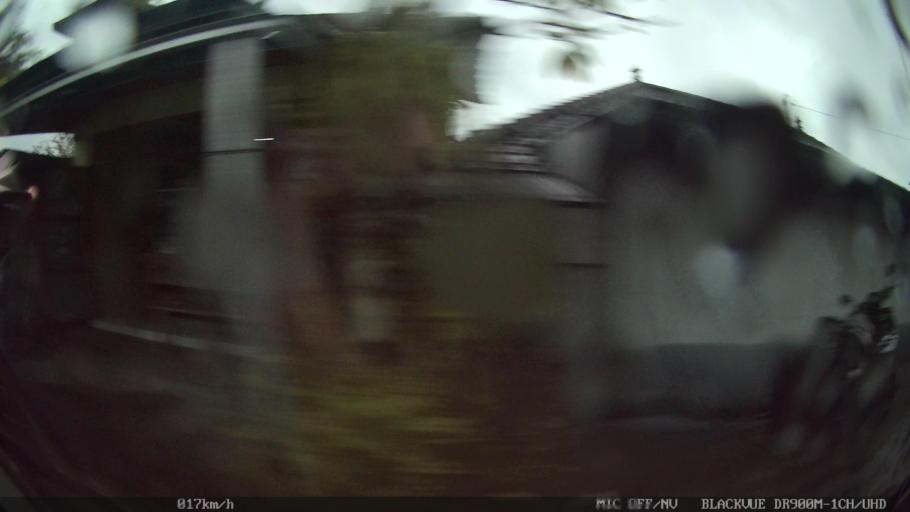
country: ID
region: Bali
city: Banjar Sedang
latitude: -8.5597
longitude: 115.2514
